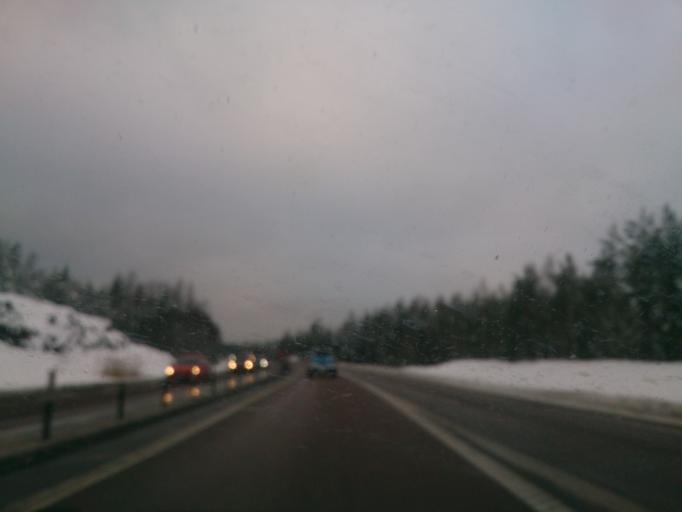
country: SE
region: Stockholm
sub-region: Varmdo Kommun
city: Gustavsberg
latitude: 59.3127
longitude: 18.3632
